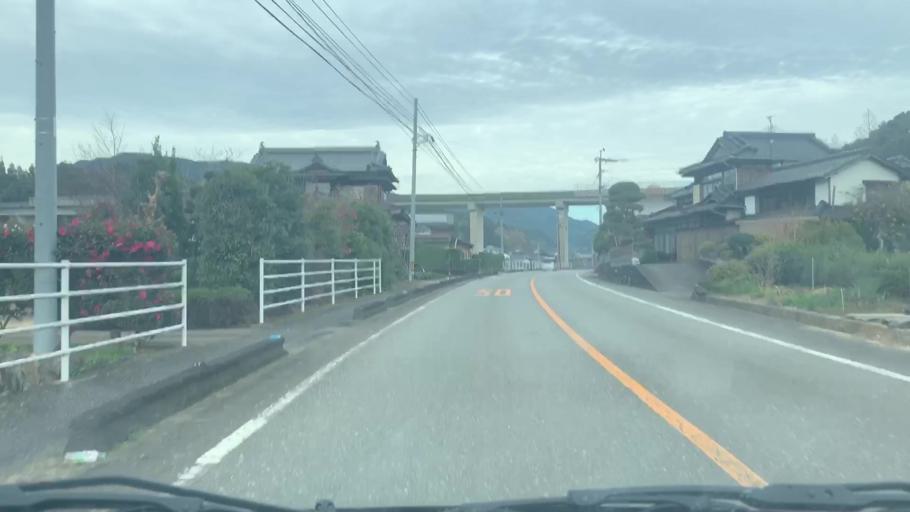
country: JP
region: Saga Prefecture
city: Ureshinomachi-shimojuku
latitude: 33.1419
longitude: 129.9771
